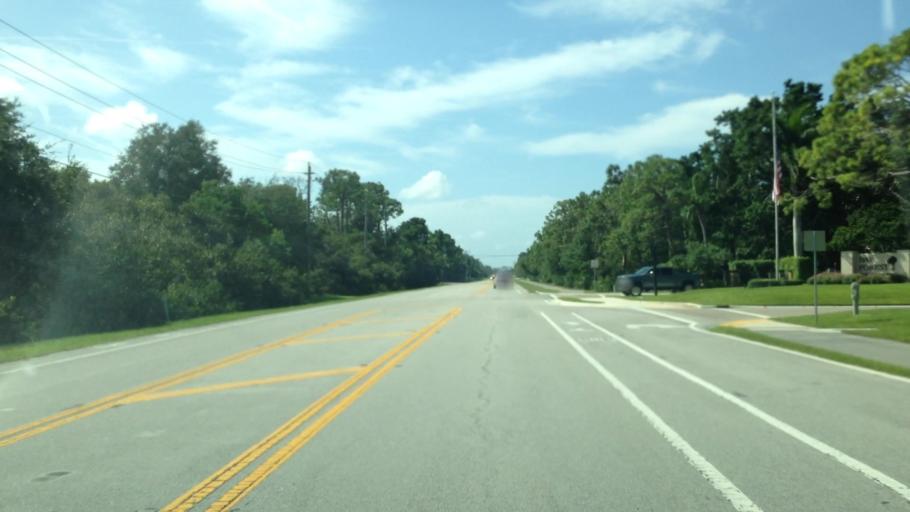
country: US
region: Florida
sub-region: Collier County
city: Naples Park
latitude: 26.3105
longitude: -81.8189
